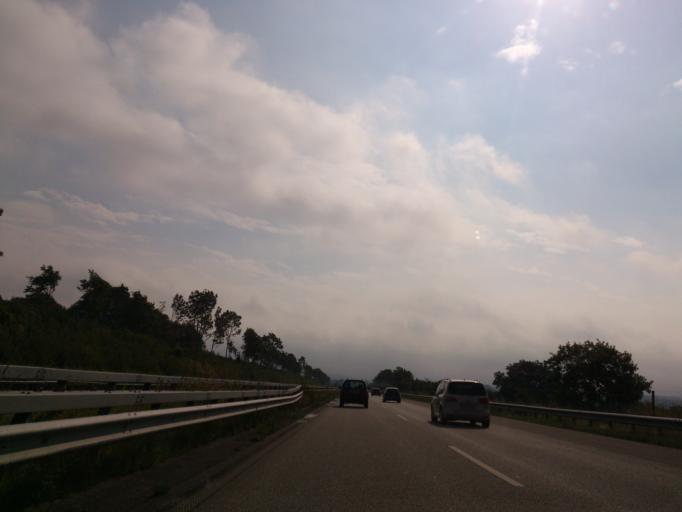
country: DE
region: Schleswig-Holstein
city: Nordhastedt
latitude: 54.1639
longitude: 9.1676
